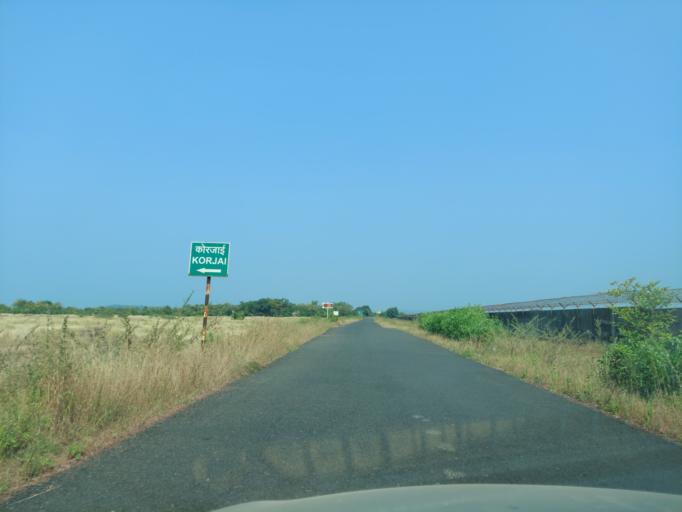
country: IN
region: Maharashtra
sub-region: Sindhudurg
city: Malvan
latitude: 15.9994
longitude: 73.5086
